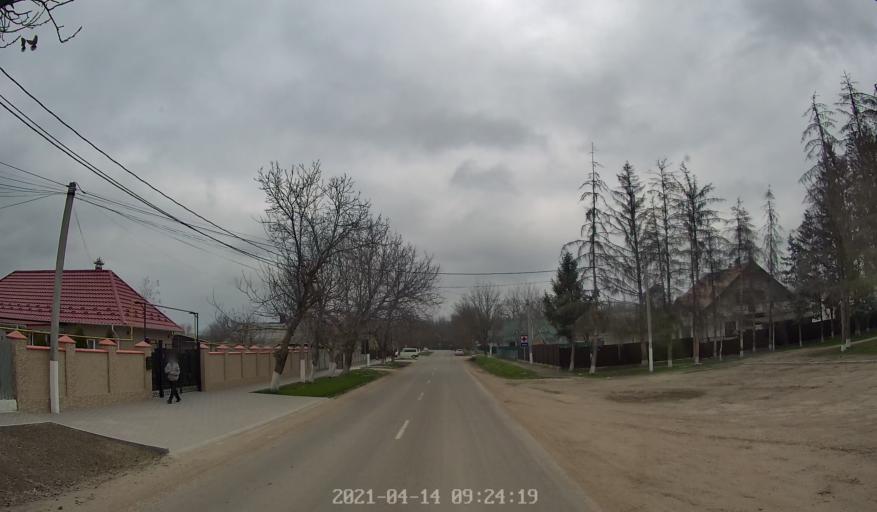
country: MD
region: Chisinau
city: Vadul lui Voda
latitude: 47.1085
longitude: 29.1144
